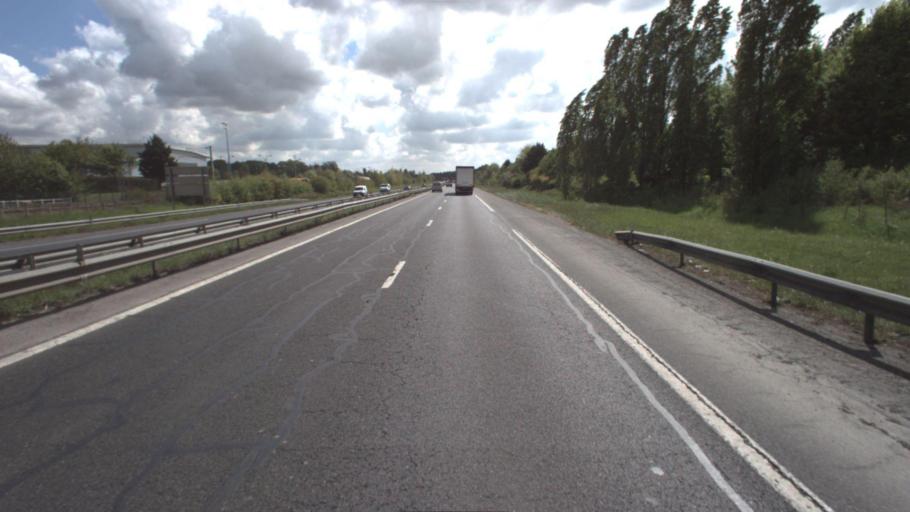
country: FR
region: Ile-de-France
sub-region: Departement de Seine-et-Marne
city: Tournan-en-Brie
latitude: 48.7316
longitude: 2.7908
